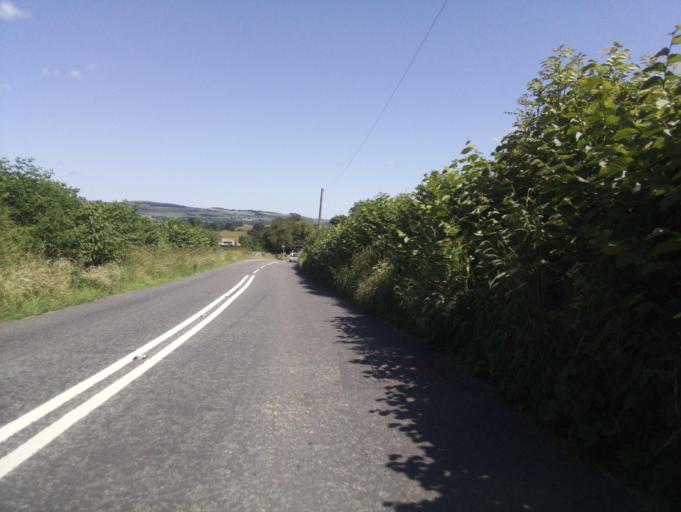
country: GB
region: England
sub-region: Derbyshire
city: Bakewell
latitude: 53.2064
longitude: -1.6928
